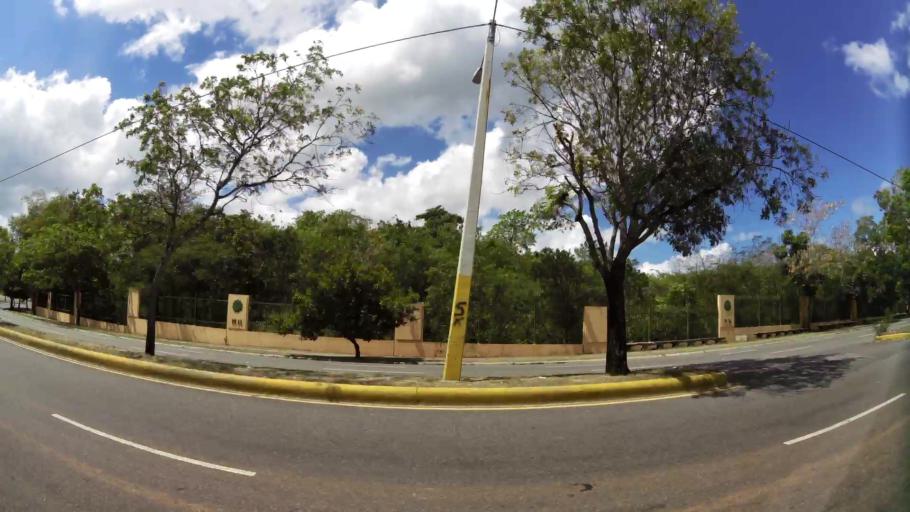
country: DO
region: Nacional
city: La Agustina
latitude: 18.5219
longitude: -69.9223
